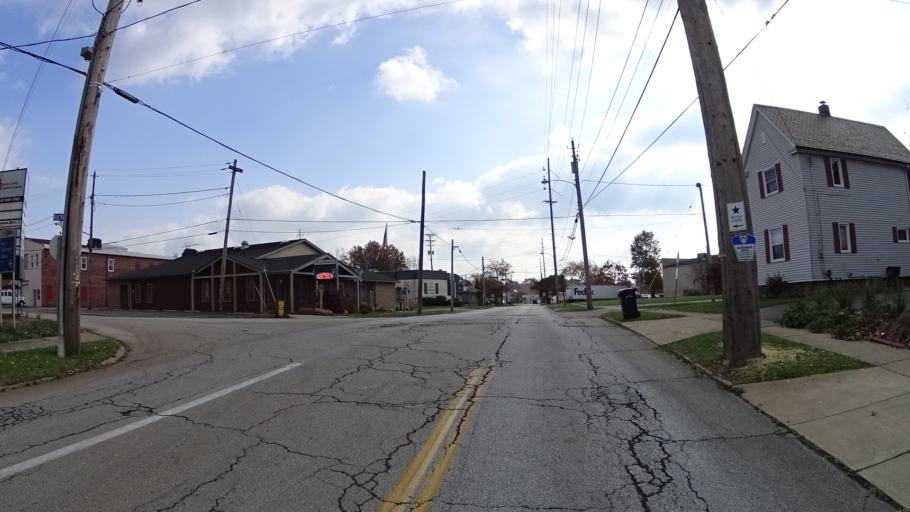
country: US
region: Ohio
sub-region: Lorain County
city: Elyria
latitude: 41.3695
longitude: -82.0970
